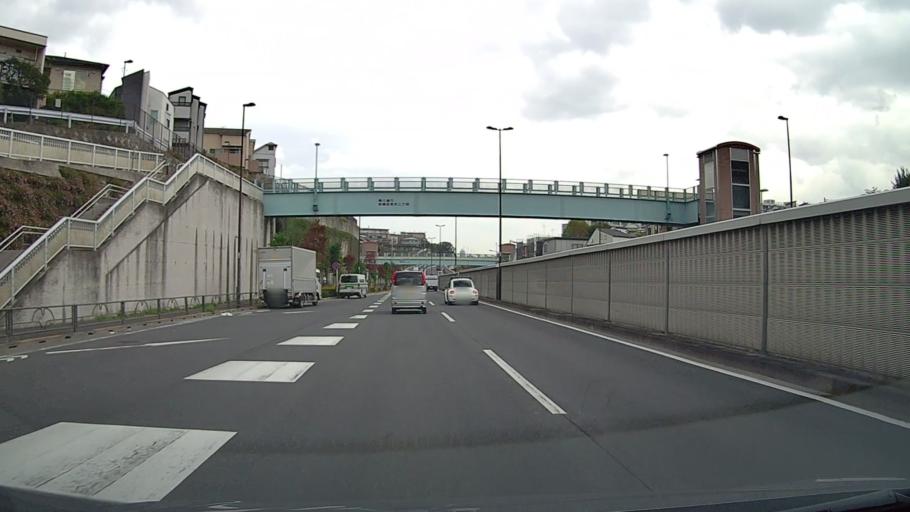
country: JP
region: Saitama
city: Shimotoda
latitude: 35.7697
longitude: 139.6700
